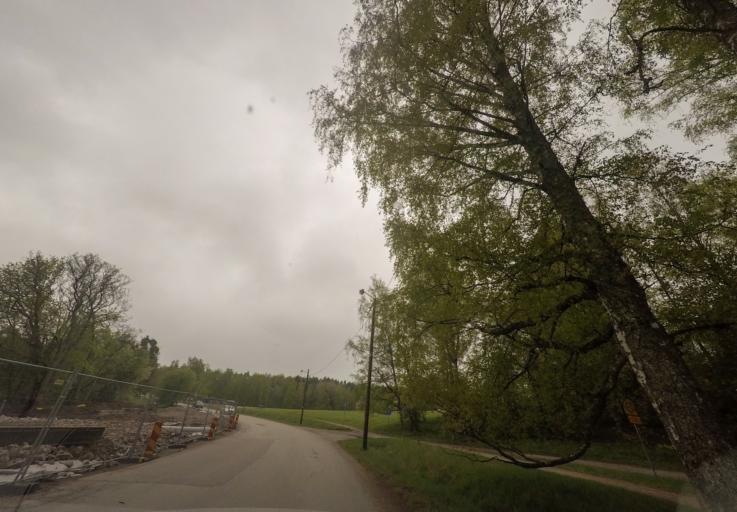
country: SE
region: Vaestmanland
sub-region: Vasteras
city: Vasteras
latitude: 59.5795
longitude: 16.6080
